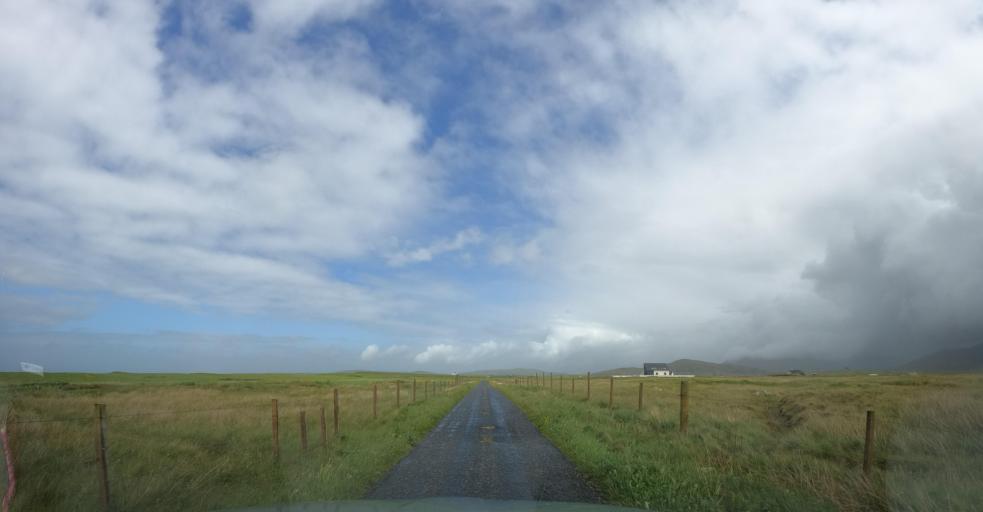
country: GB
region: Scotland
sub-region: Eilean Siar
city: Isle of South Uist
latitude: 57.2901
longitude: -7.4086
